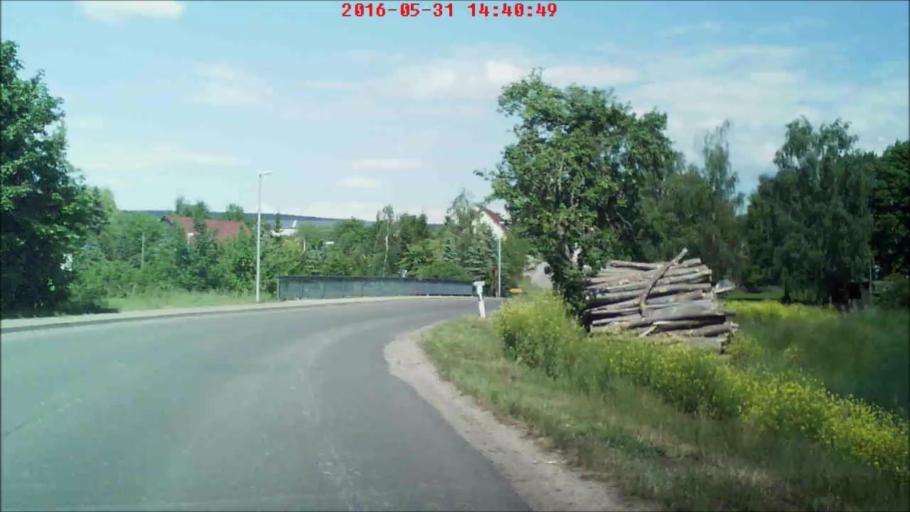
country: DE
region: Thuringia
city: Bilzingsleben
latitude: 51.2821
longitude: 11.0706
